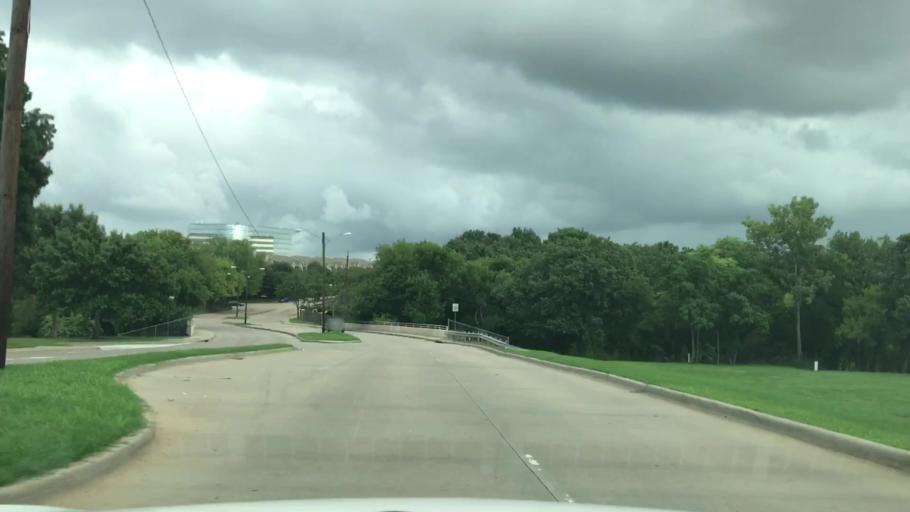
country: US
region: Texas
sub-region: Dallas County
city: Richardson
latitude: 32.9175
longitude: -96.7528
